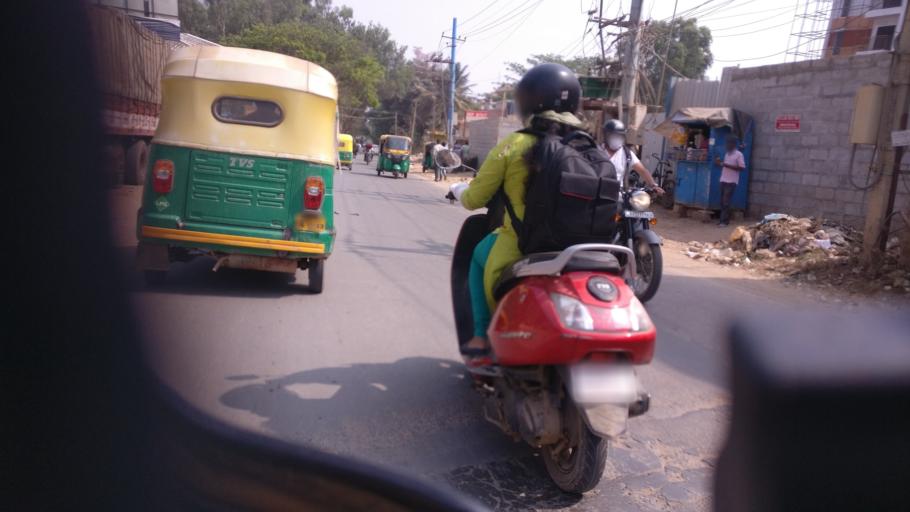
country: IN
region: Karnataka
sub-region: Bangalore Urban
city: Bangalore
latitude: 12.8928
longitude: 77.6738
